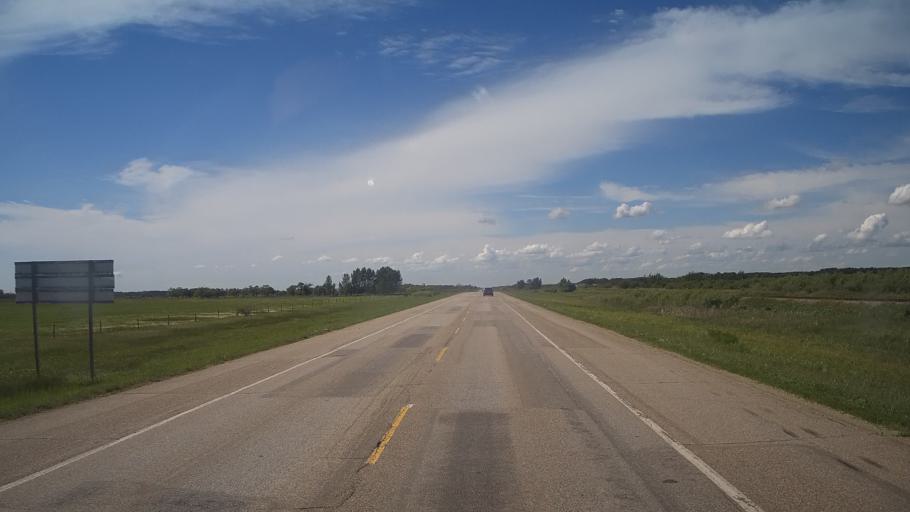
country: CA
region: Saskatchewan
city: Yorkton
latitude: 51.0565
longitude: -102.1957
